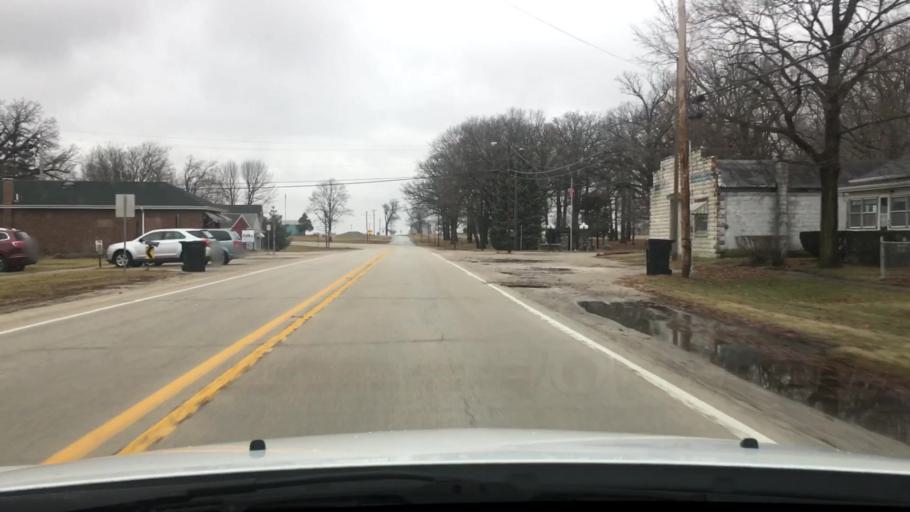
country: US
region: Illinois
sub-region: Iroquois County
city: Sheldon
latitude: 40.8268
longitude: -87.5816
